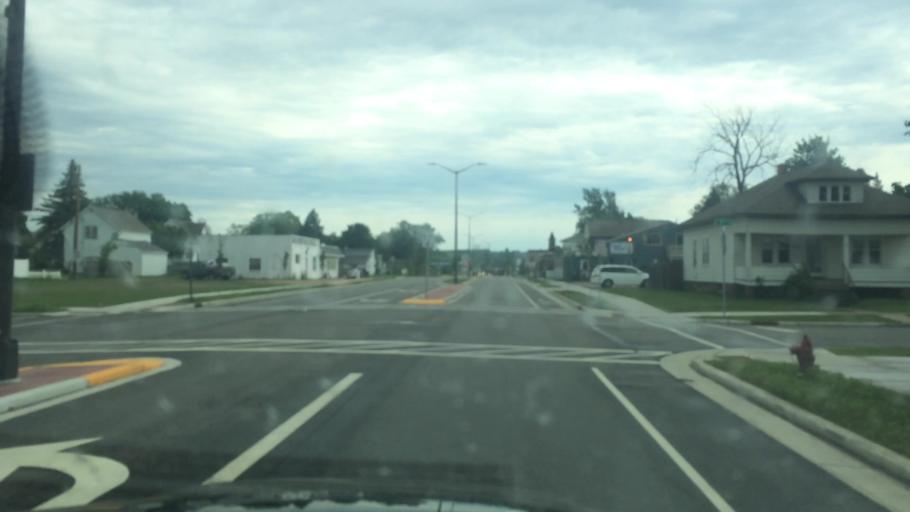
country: US
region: Wisconsin
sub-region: Marathon County
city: Wausau
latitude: 44.9483
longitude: -89.6445
